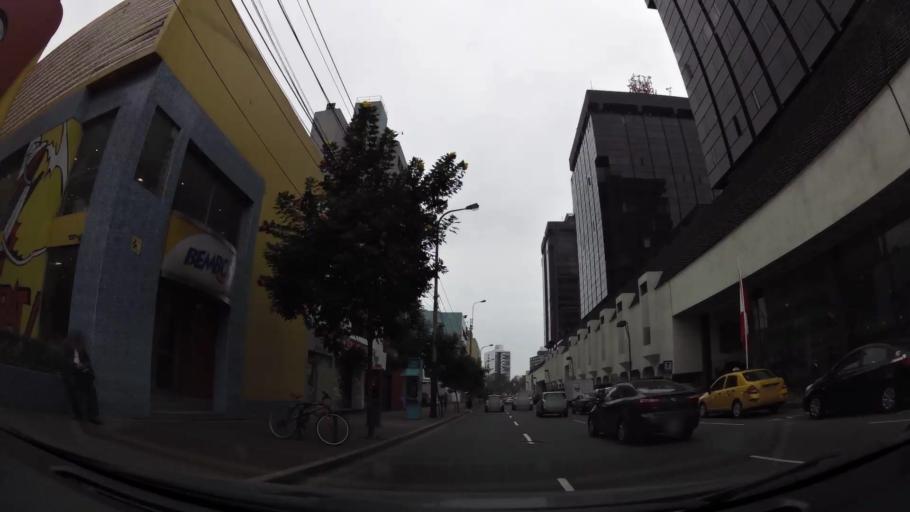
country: PE
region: Lima
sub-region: Lima
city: San Isidro
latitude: -12.0970
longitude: -77.0360
